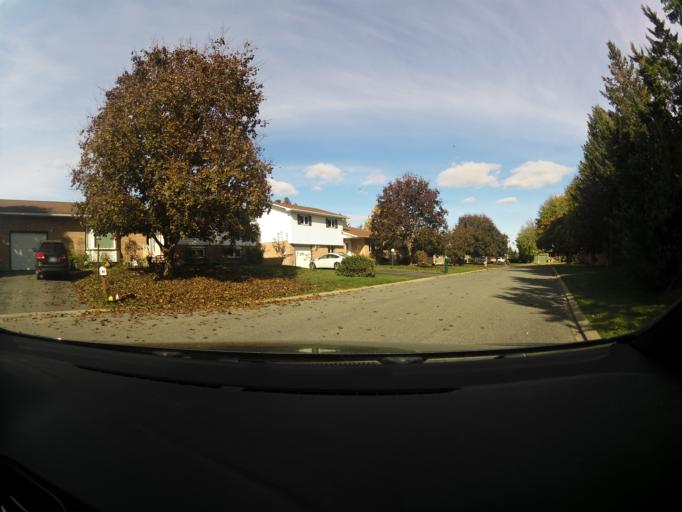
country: CA
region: Ontario
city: Bells Corners
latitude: 45.2805
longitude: -75.9228
